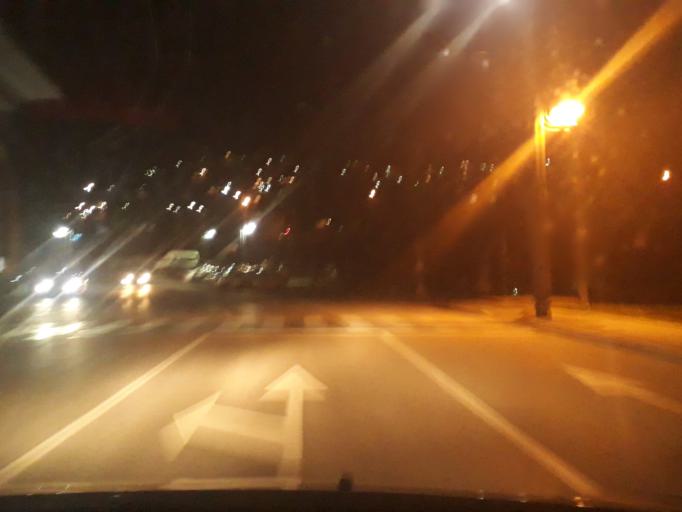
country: BA
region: Federation of Bosnia and Herzegovina
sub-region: Kanton Sarajevo
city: Sarajevo
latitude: 43.8474
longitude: 18.3734
